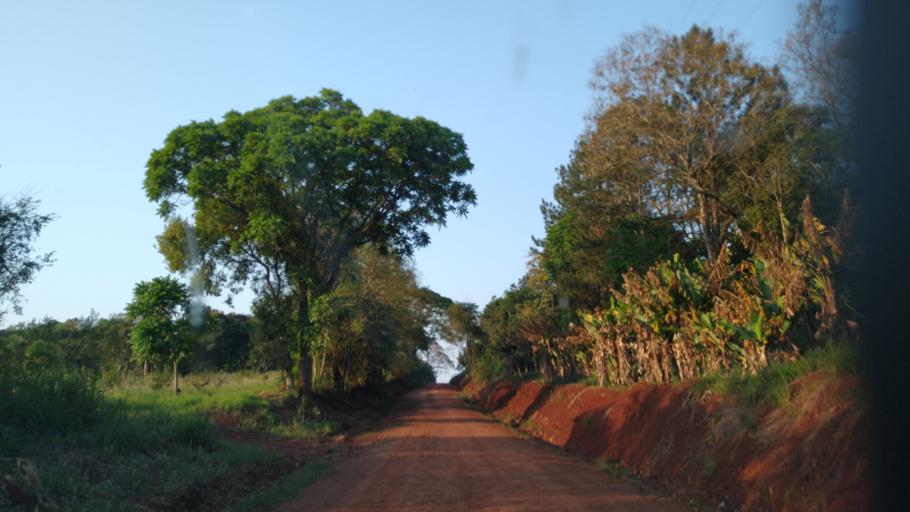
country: AR
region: Misiones
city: Jardin America
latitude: -27.0839
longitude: -55.2752
